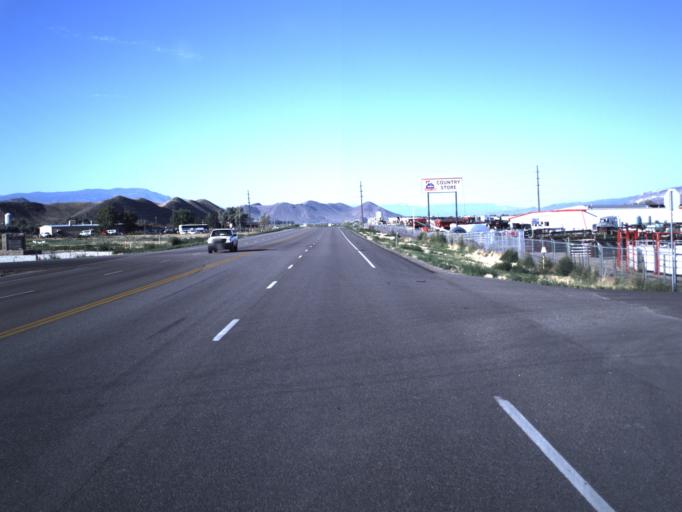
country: US
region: Utah
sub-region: Sevier County
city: Salina
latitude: 38.9524
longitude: -111.8763
